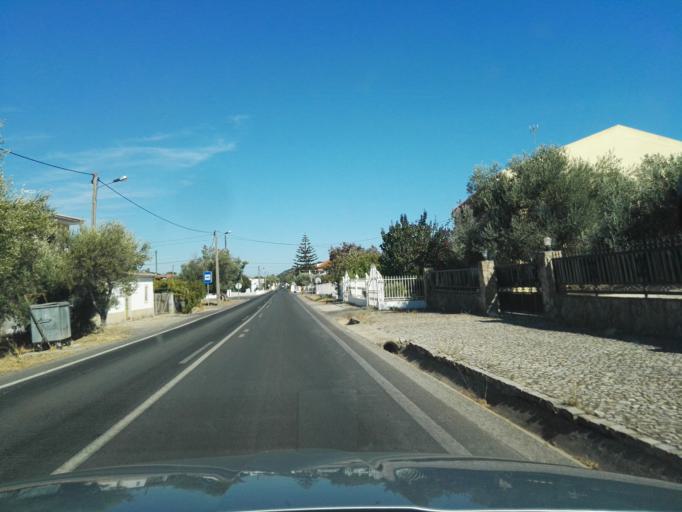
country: PT
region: Faro
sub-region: Sao Bras de Alportel
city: Sao Bras de Alportel
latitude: 37.1546
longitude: -7.8617
